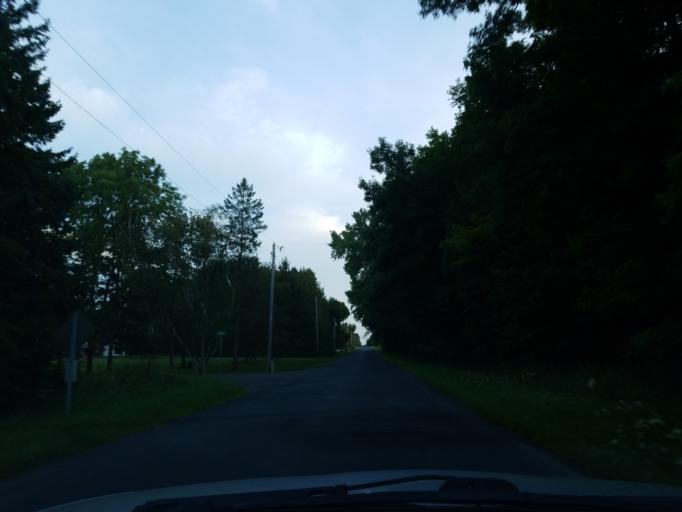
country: US
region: Minnesota
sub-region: Washington County
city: Stillwater
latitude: 45.0858
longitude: -92.7713
